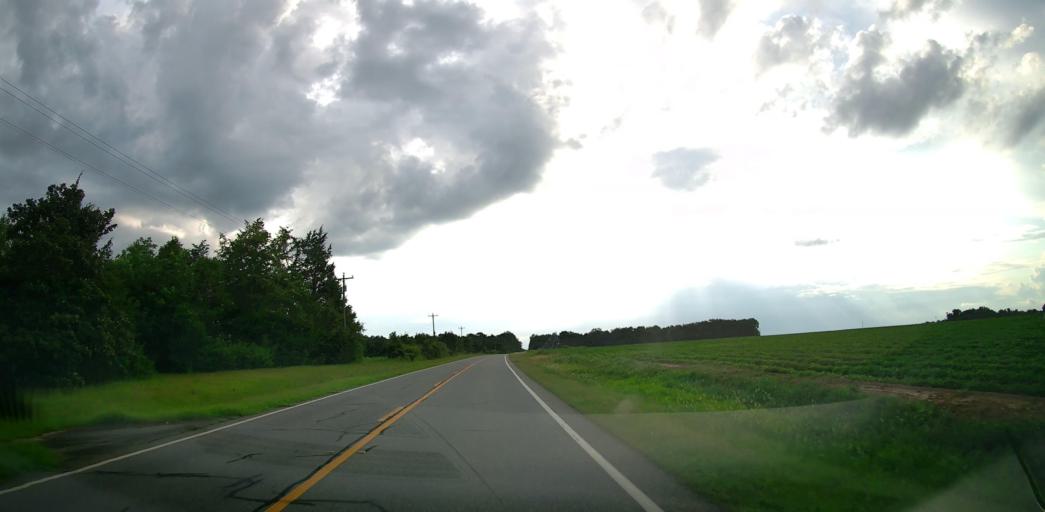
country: US
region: Georgia
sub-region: Pulaski County
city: Hawkinsville
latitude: 32.2955
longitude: -83.5417
